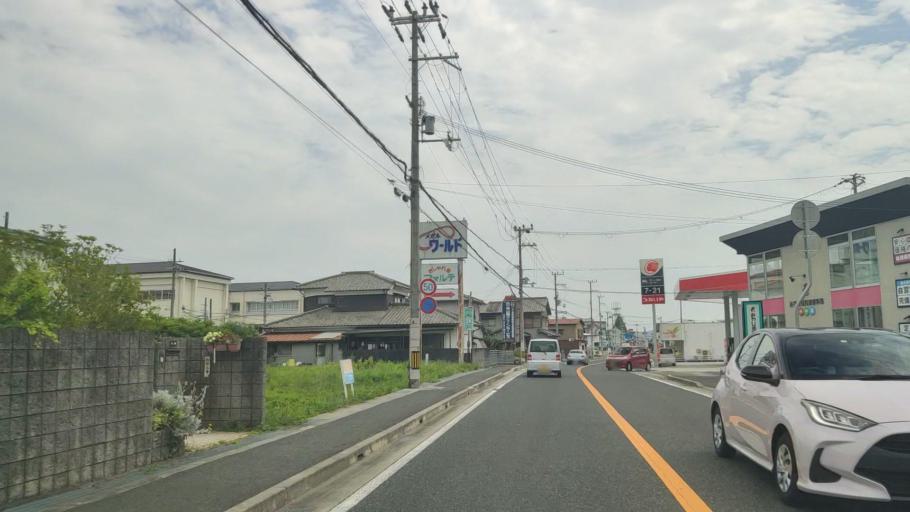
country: JP
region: Hyogo
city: Tatsunocho-tominaga
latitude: 34.8689
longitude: 134.5541
